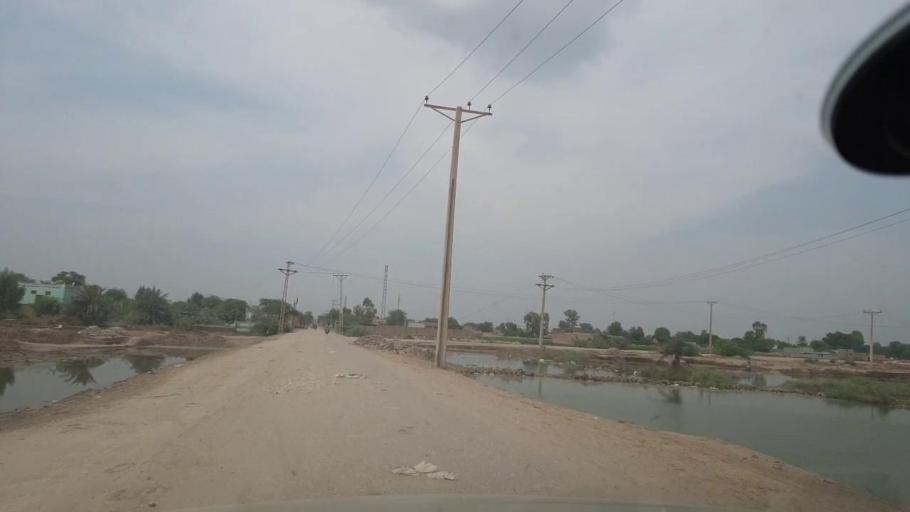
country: PK
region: Sindh
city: Jacobabad
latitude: 28.2618
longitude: 68.4374
